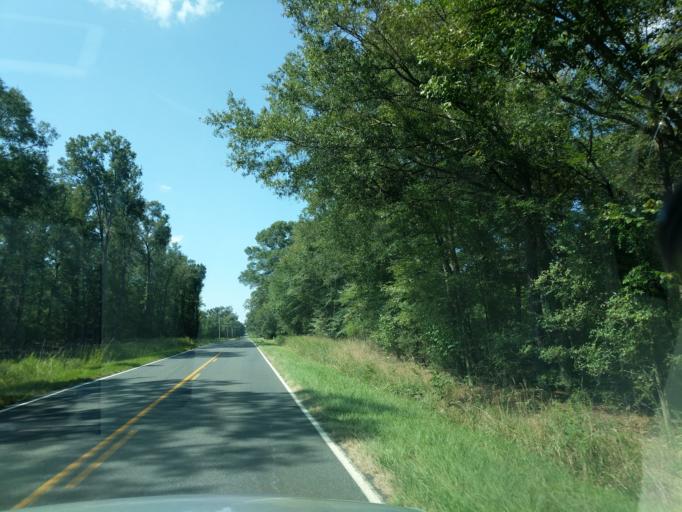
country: US
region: South Carolina
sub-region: Lexington County
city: Leesville
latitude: 34.0314
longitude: -81.5360
